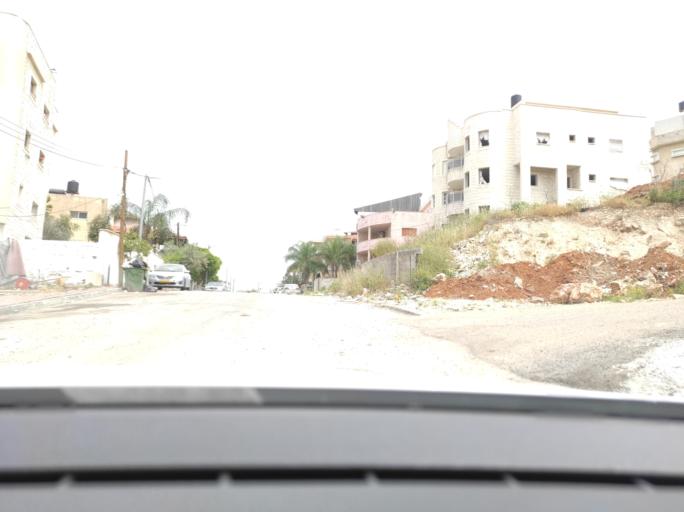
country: IL
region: Central District
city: Kafr Qasim
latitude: 32.1165
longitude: 34.9648
